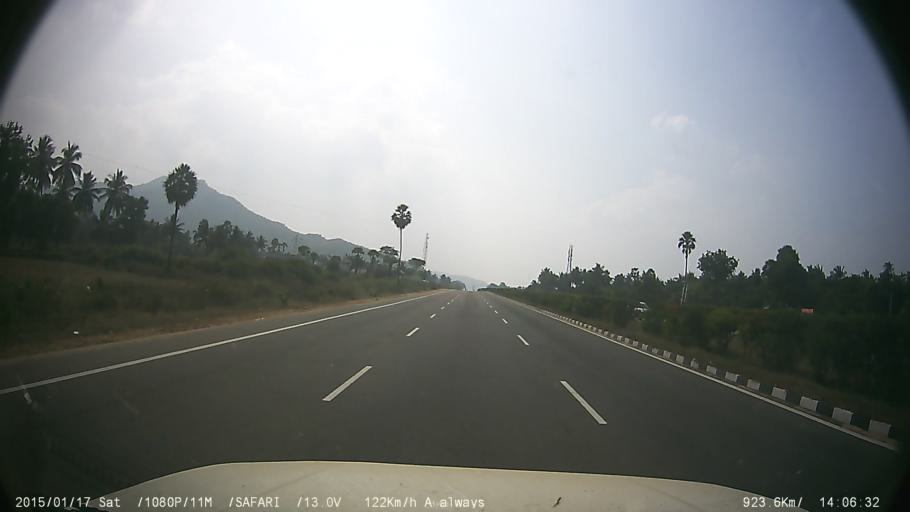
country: IN
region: Tamil Nadu
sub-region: Vellore
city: Ambur
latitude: 12.8384
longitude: 78.7911
